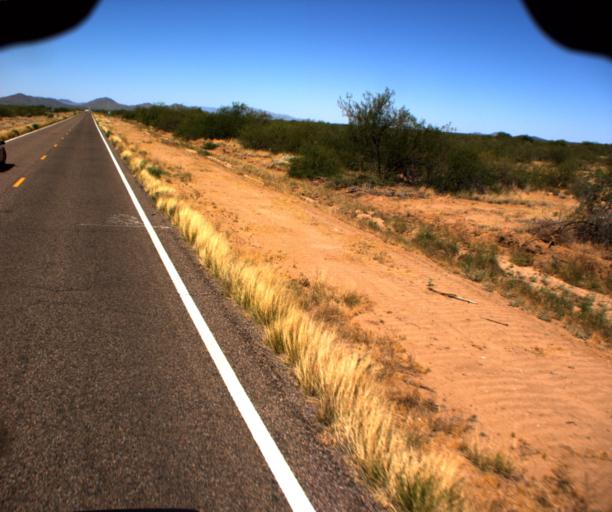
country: US
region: Arizona
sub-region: Yavapai County
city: Congress
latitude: 34.1496
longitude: -112.8845
